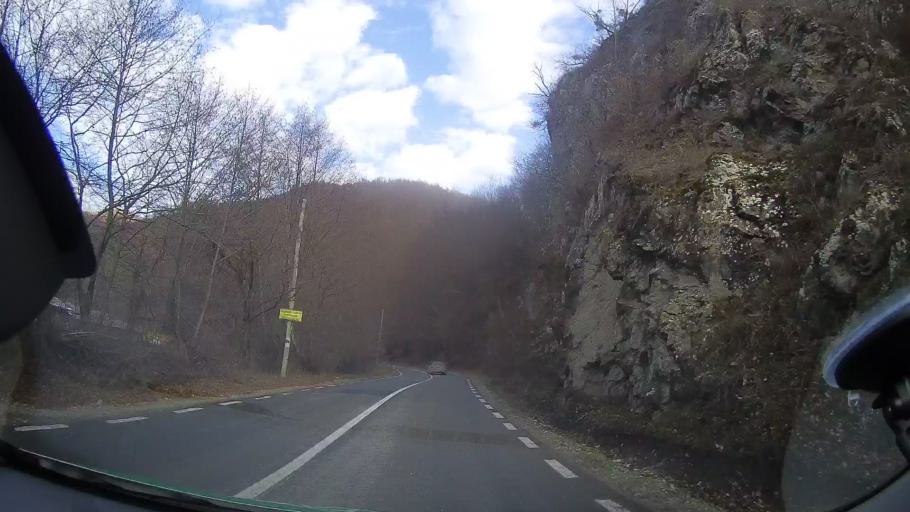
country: RO
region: Cluj
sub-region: Comuna Baisoara
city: Baisoara
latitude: 46.6066
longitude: 23.4187
